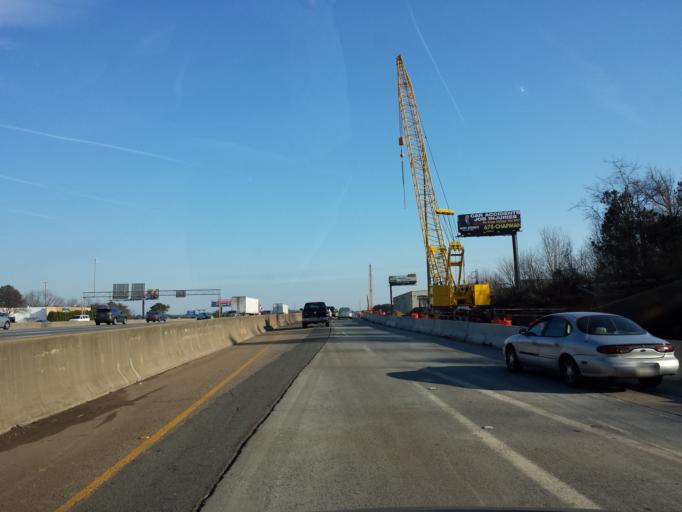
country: US
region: Georgia
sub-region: Cobb County
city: Marietta
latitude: 33.9811
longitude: -84.5392
